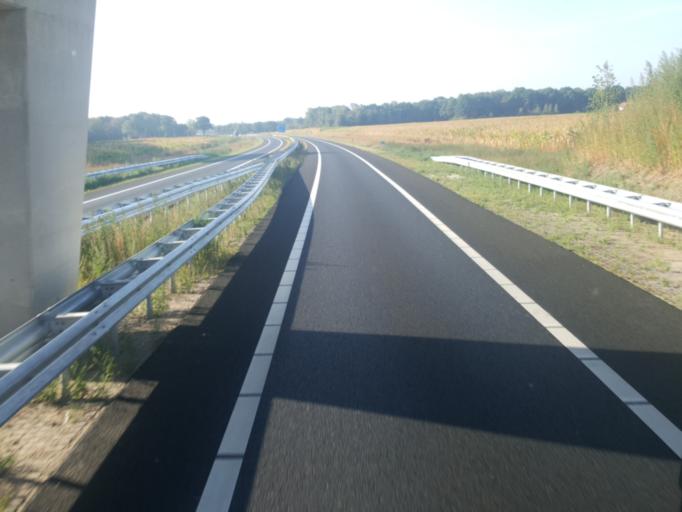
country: NL
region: Gelderland
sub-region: Berkelland
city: Eibergen
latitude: 52.0980
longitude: 6.6204
